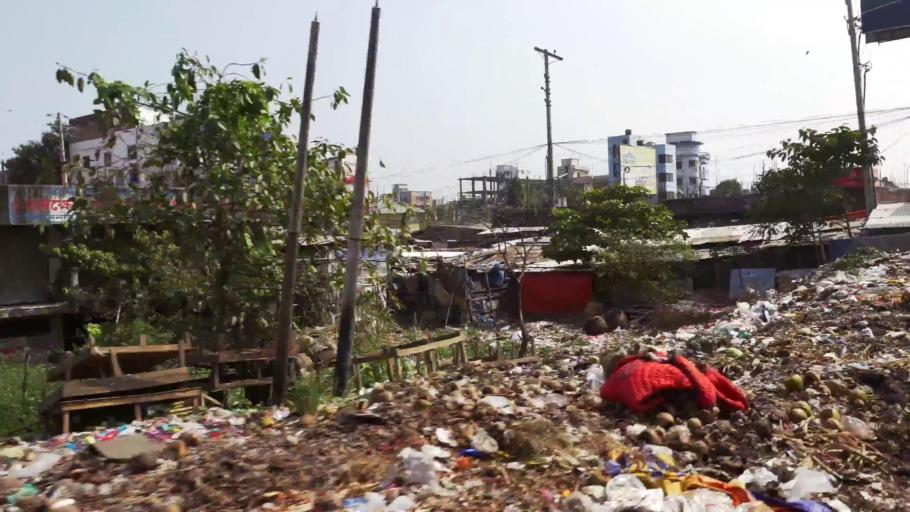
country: BD
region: Dhaka
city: Tungi
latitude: 23.8853
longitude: 90.4068
